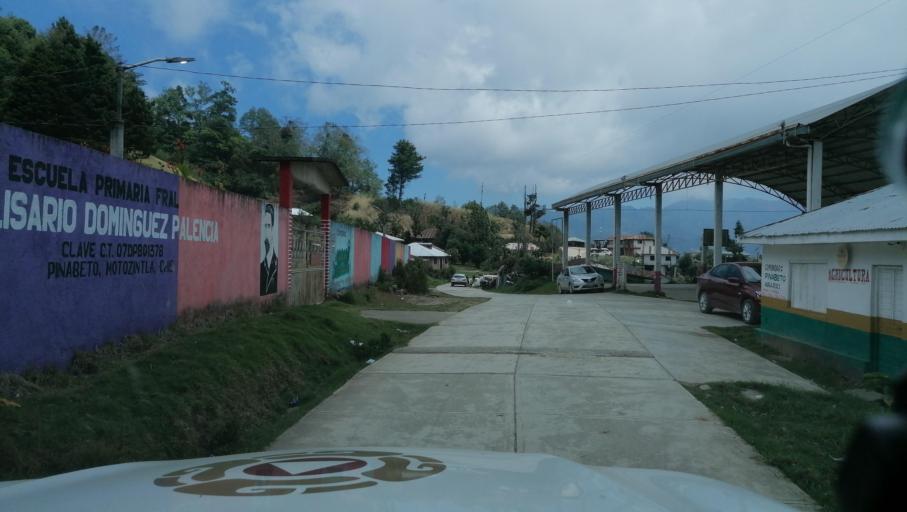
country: MX
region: Chiapas
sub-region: Tapachula
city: Canton Villaflor
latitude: 15.2137
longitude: -92.2389
